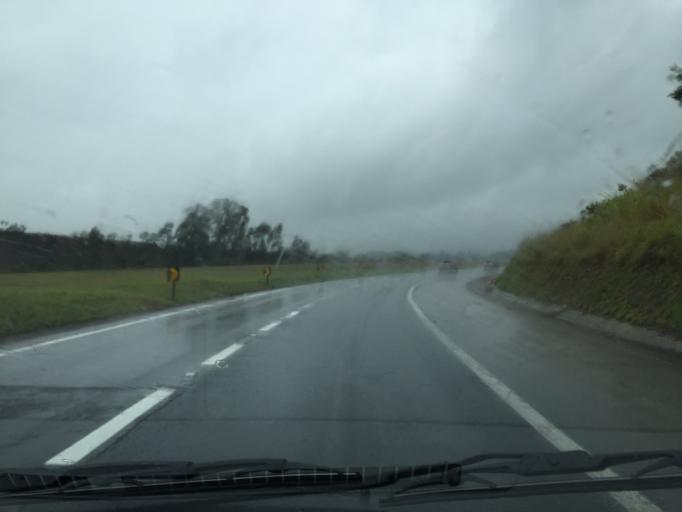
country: BR
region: Sao Paulo
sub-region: Itu
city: Itu
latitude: -23.4022
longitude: -47.3341
